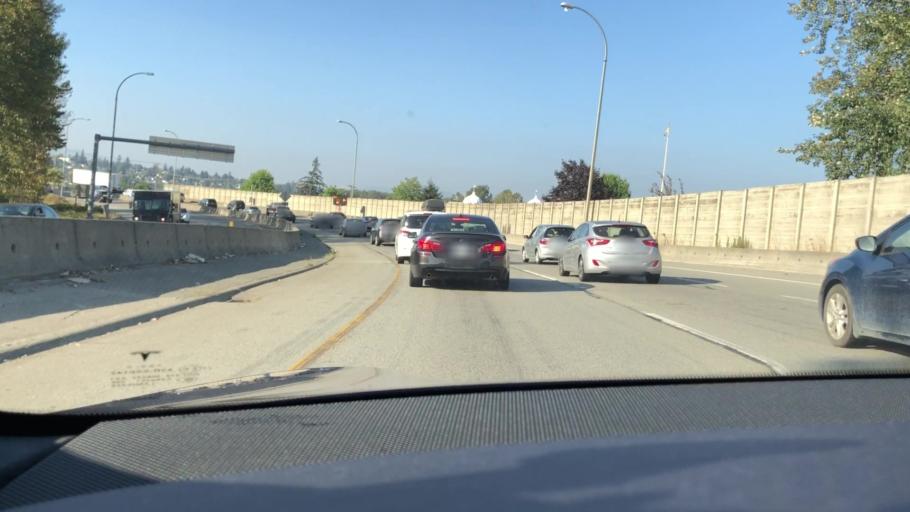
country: CA
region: British Columbia
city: New Westminster
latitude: 49.1904
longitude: -122.9426
